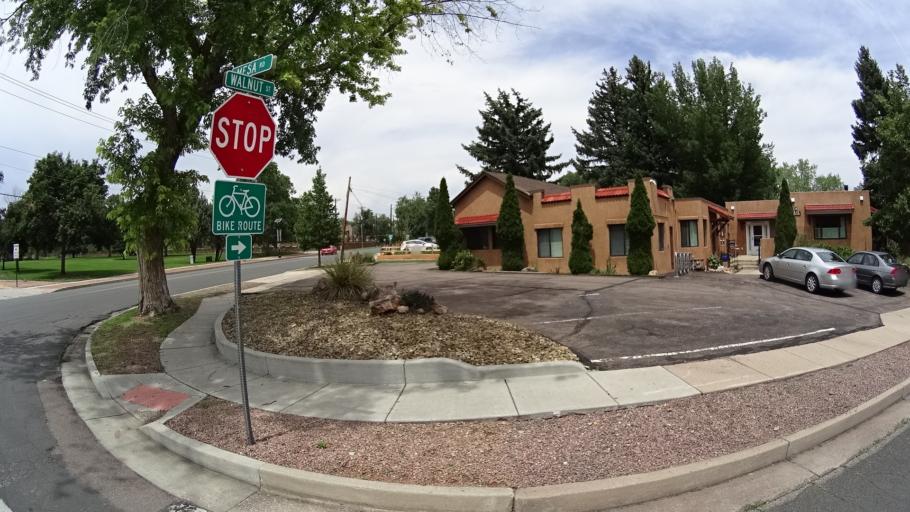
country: US
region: Colorado
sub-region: El Paso County
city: Colorado Springs
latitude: 38.8462
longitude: -104.8333
